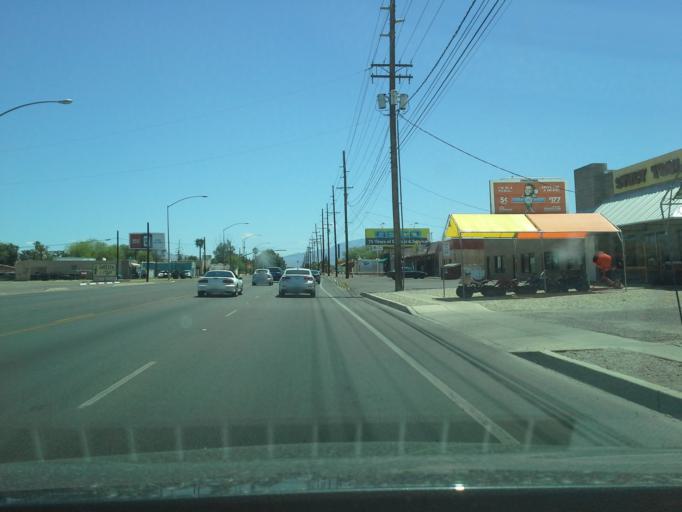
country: US
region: Arizona
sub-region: Pima County
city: Tucson
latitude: 32.2506
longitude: -110.9051
